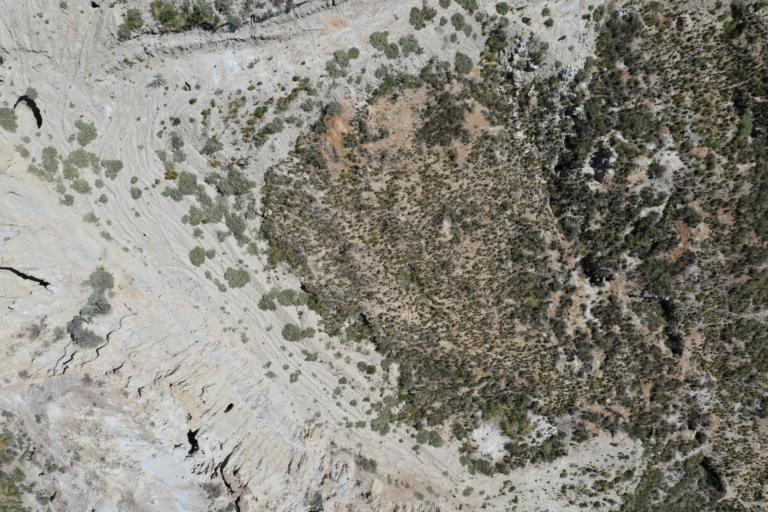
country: BO
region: La Paz
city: La Paz
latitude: -16.5569
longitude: -68.1227
